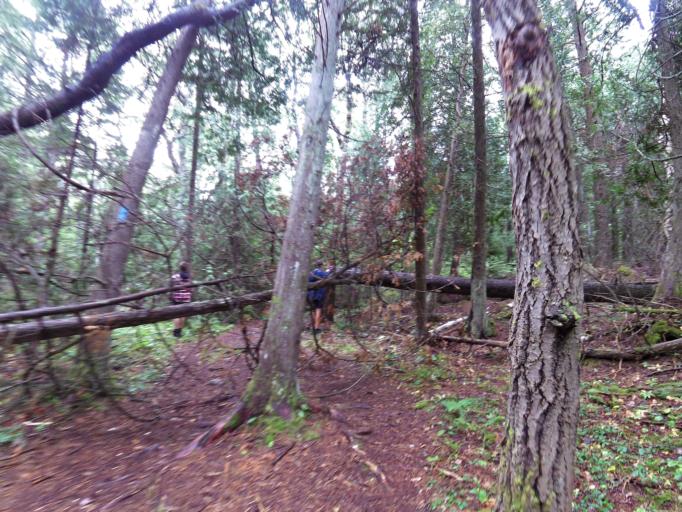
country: CA
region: Ontario
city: Tobermory
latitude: 45.2595
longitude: -81.6480
